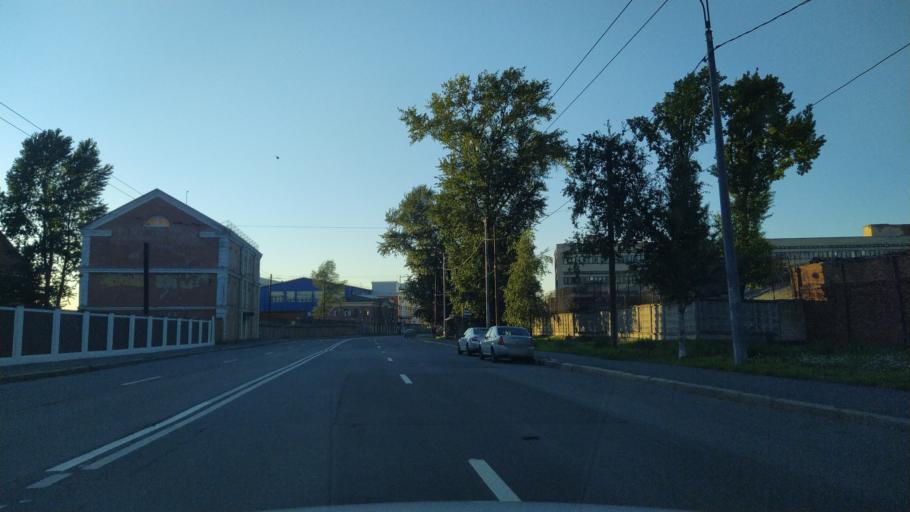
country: RU
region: Leningrad
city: Finlyandskiy
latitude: 59.9596
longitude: 30.3700
